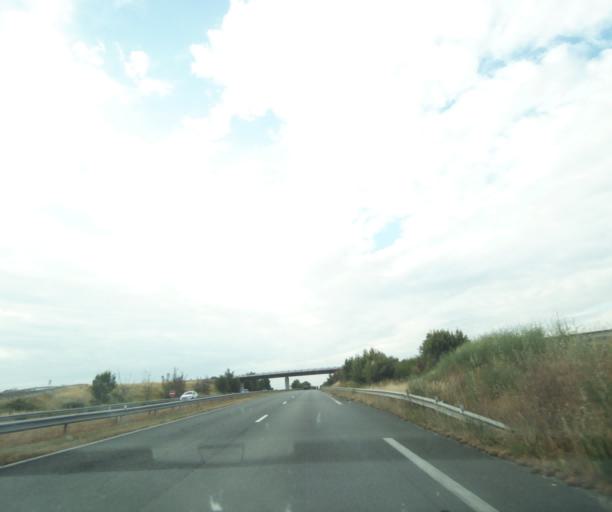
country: FR
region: Poitou-Charentes
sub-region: Departement de la Charente-Maritime
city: Chatelaillon-Plage
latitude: 46.0622
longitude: -1.0614
